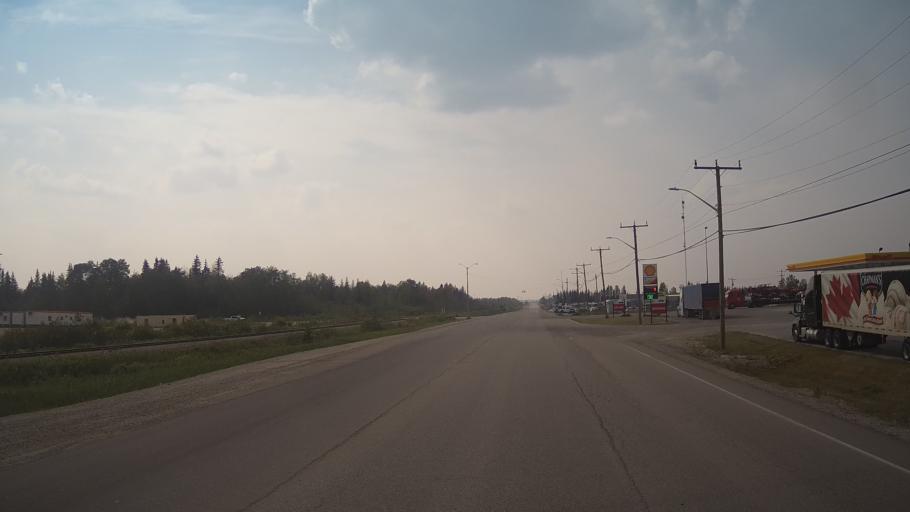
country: CA
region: Ontario
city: Kapuskasing
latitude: 49.3965
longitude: -82.3688
